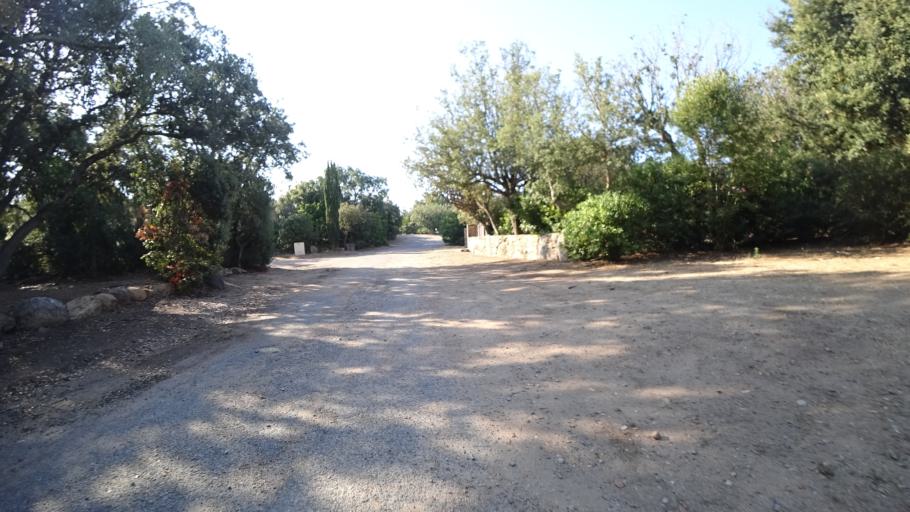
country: FR
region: Corsica
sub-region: Departement de la Corse-du-Sud
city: Porto-Vecchio
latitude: 41.6216
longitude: 9.3418
